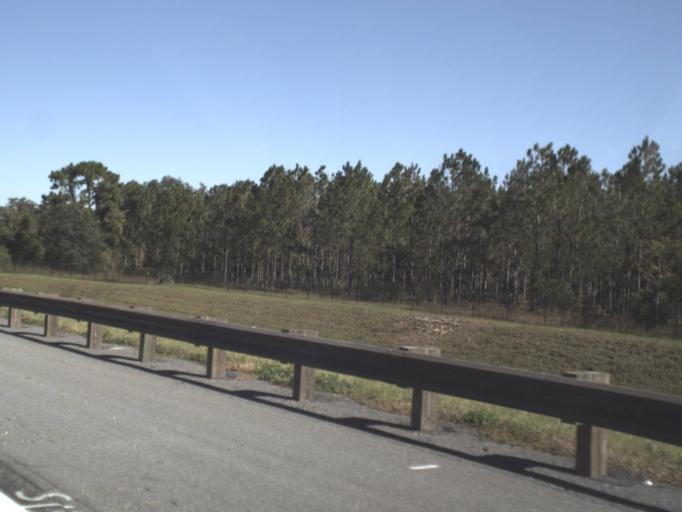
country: US
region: Florida
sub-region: Pasco County
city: Shady Hills
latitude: 28.3526
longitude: -82.5448
